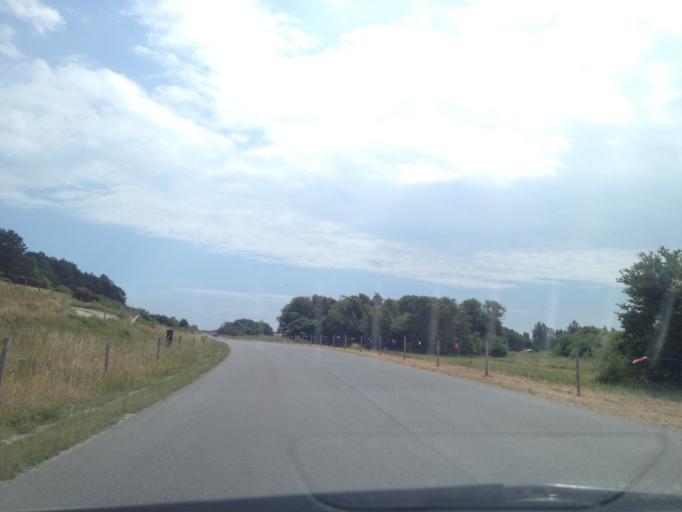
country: DK
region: Central Jutland
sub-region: Syddjurs Kommune
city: Ebeltoft
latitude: 56.1558
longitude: 10.6787
